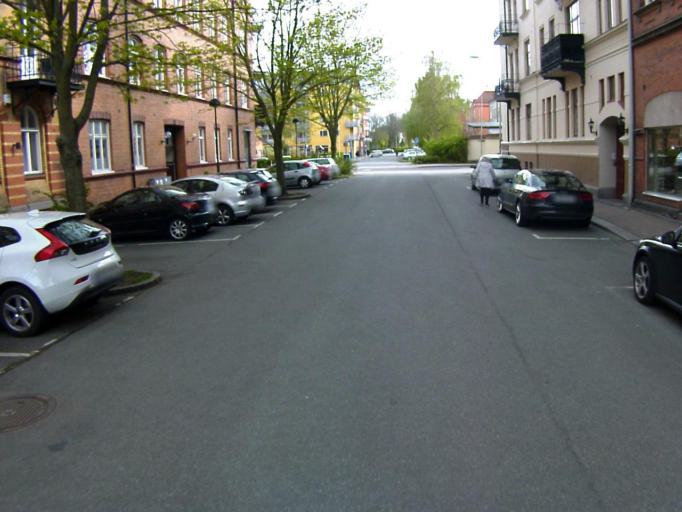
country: SE
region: Skane
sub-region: Kristianstads Kommun
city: Kristianstad
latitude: 56.0320
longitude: 14.1631
